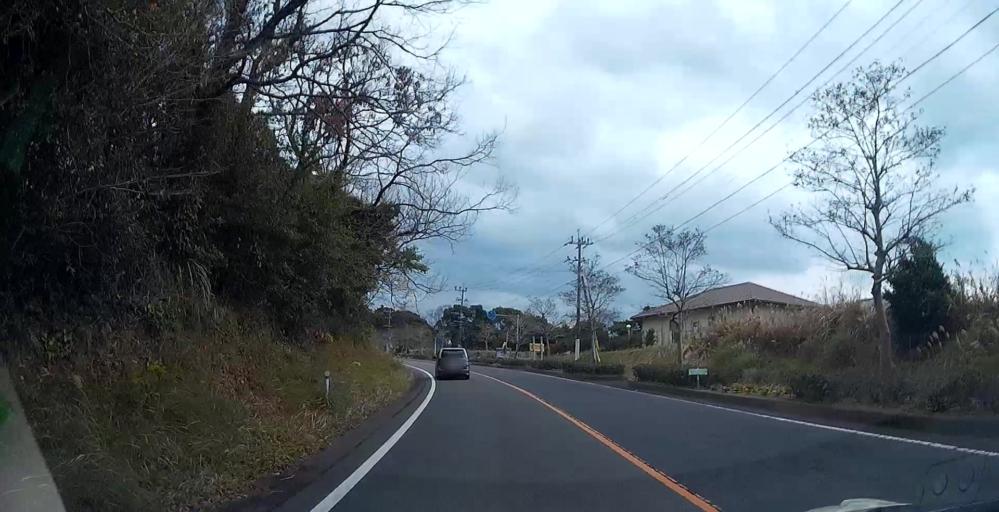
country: JP
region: Kagoshima
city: Akune
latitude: 32.0783
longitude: 130.2051
